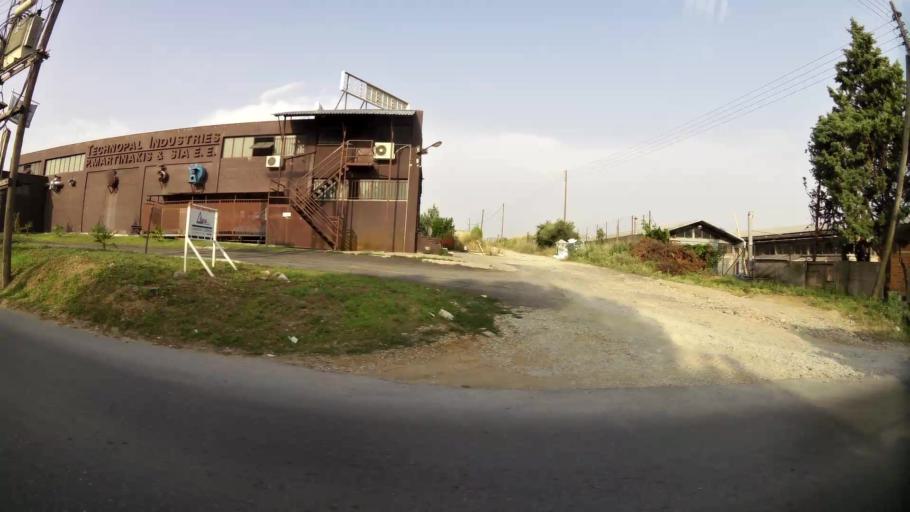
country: GR
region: Central Macedonia
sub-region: Nomos Thessalonikis
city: Evosmos
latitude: 40.6855
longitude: 22.9060
